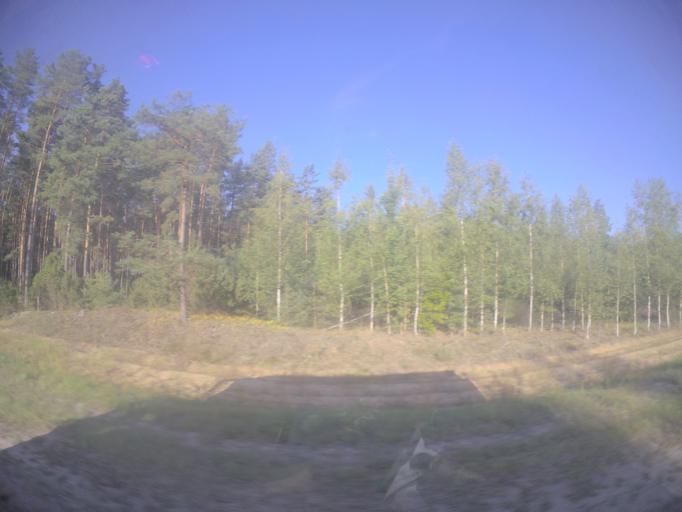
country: LT
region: Alytaus apskritis
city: Druskininkai
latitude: 53.8551
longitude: 23.8913
